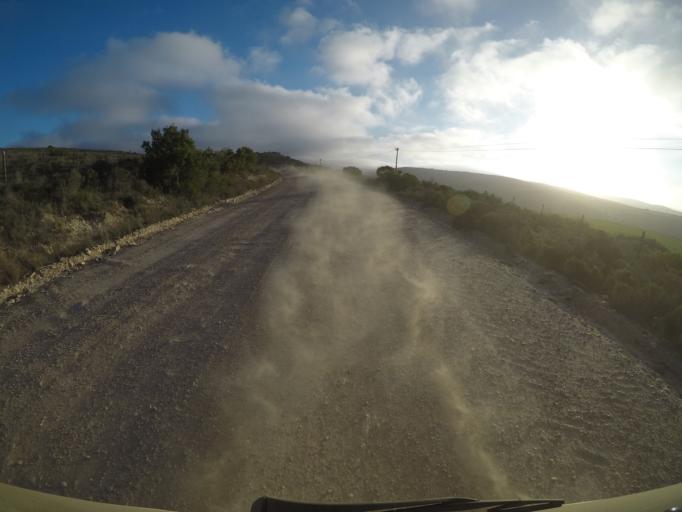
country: ZA
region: Western Cape
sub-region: Eden District Municipality
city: Mossel Bay
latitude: -34.1274
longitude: 22.0491
